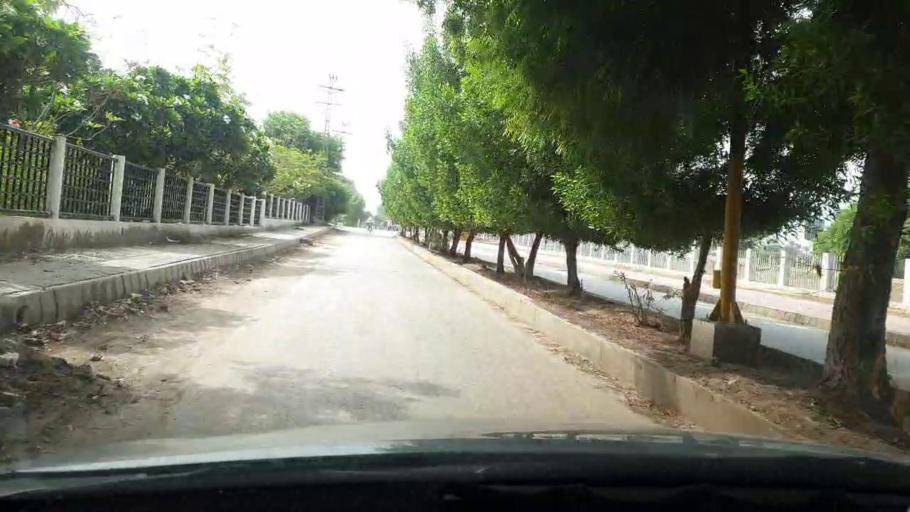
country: PK
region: Sindh
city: Khairpur
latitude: 27.5157
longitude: 68.7596
